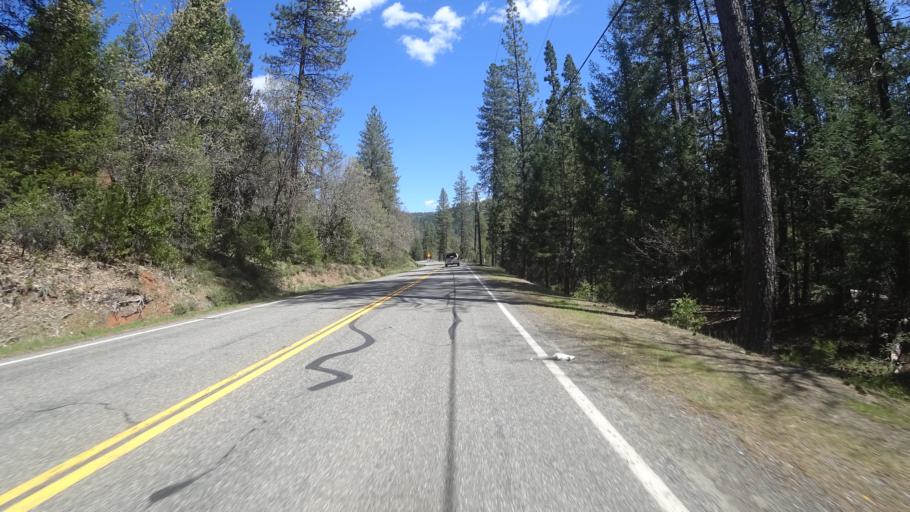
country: US
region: California
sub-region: Trinity County
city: Weaverville
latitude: 40.7517
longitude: -122.8999
